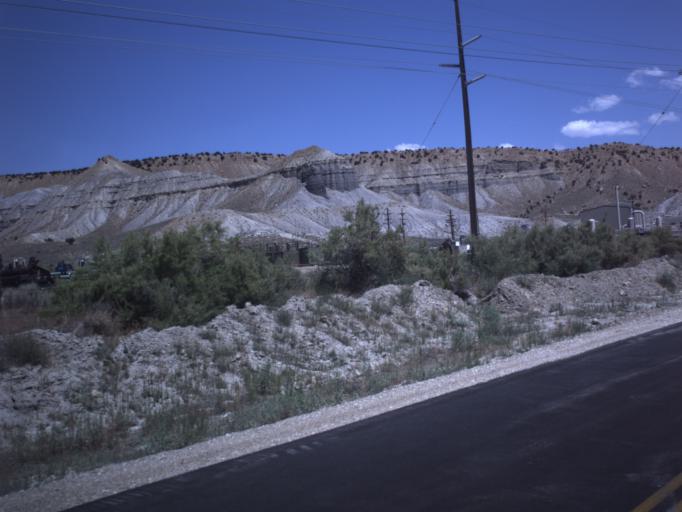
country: US
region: Utah
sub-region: Emery County
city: Orangeville
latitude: 39.2609
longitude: -111.1136
